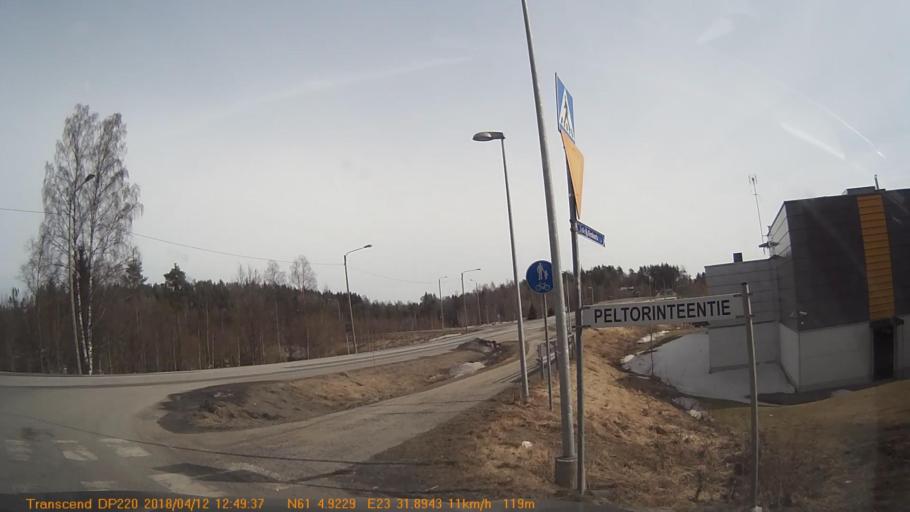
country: FI
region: Pirkanmaa
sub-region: Etelae-Pirkanmaa
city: Urjala
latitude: 61.0820
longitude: 23.5315
